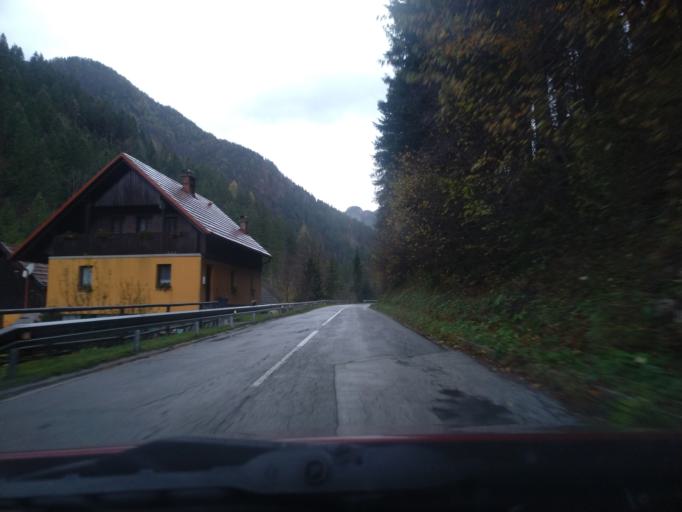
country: SI
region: Solcava
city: Solcava
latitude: 46.4016
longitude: 14.7058
